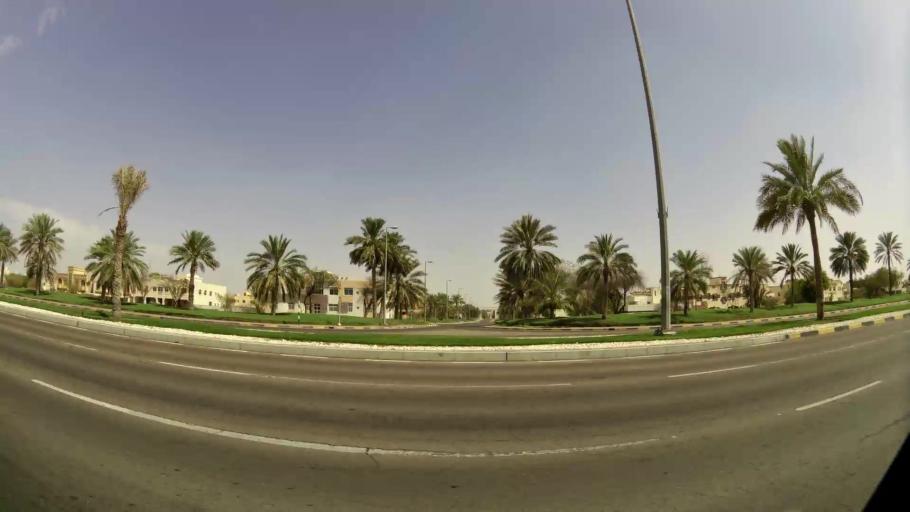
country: AE
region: Abu Dhabi
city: Al Ain
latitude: 24.2203
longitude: 55.6925
